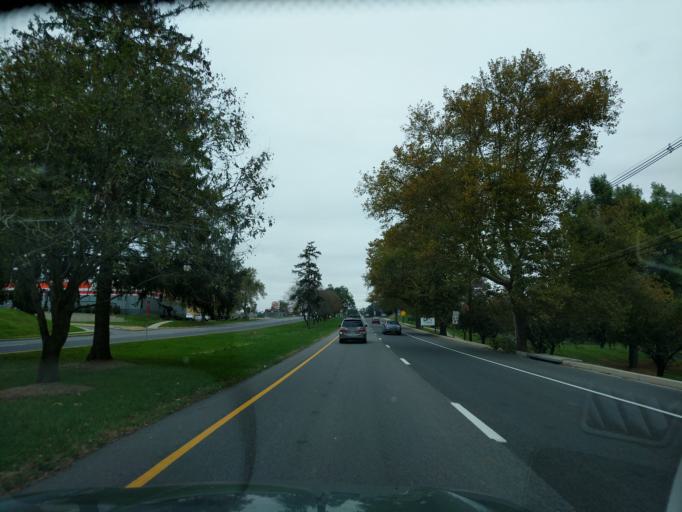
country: US
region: Maryland
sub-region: Washington County
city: Hagerstown
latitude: 39.6356
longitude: -77.7058
